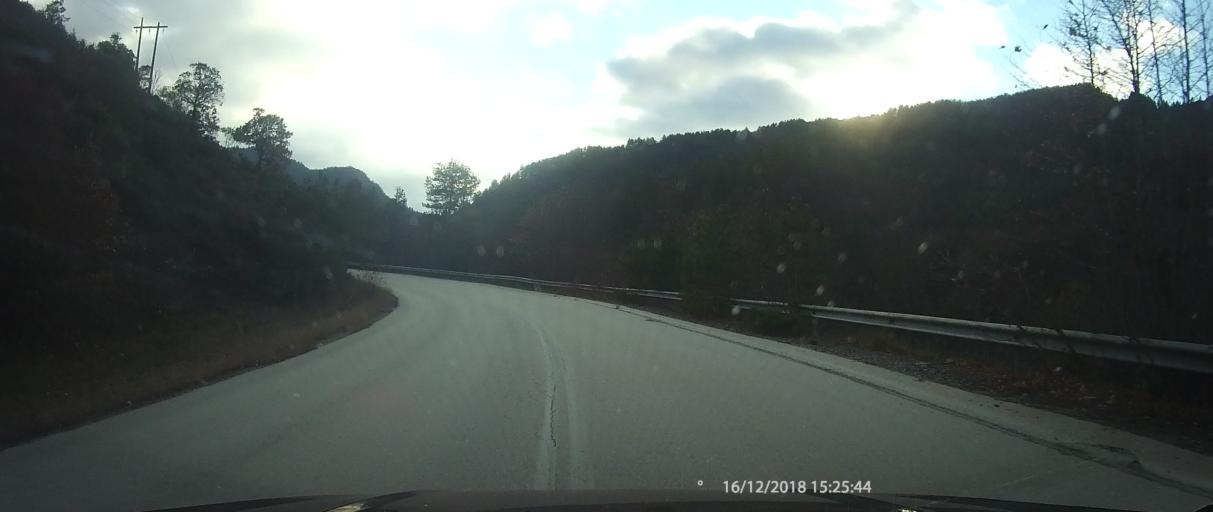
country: GR
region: Epirus
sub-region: Nomos Ioanninon
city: Konitsa
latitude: 40.1245
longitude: 20.7812
